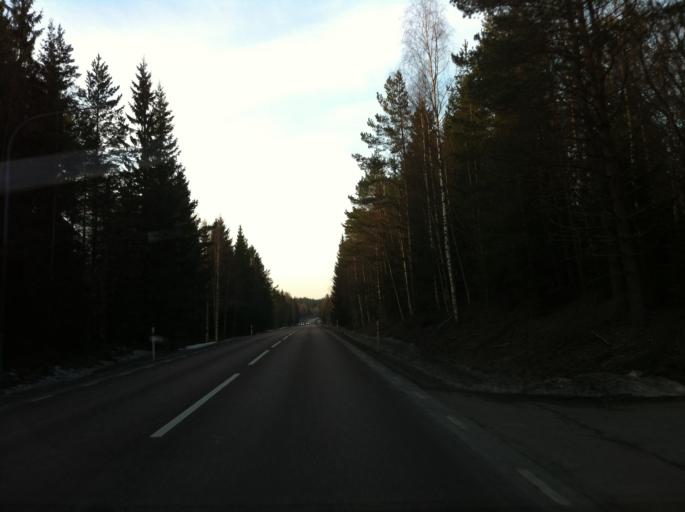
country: SE
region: Vaermland
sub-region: Filipstads Kommun
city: Lesjofors
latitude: 59.9975
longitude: 14.1626
